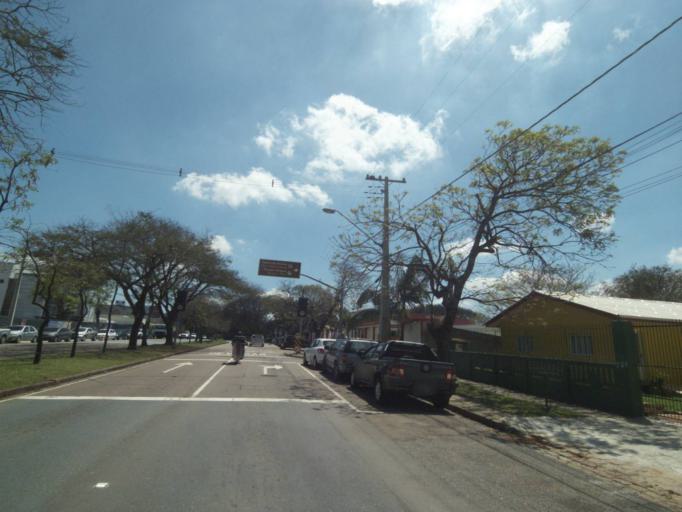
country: BR
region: Parana
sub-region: Curitiba
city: Curitiba
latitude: -25.4100
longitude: -49.2410
